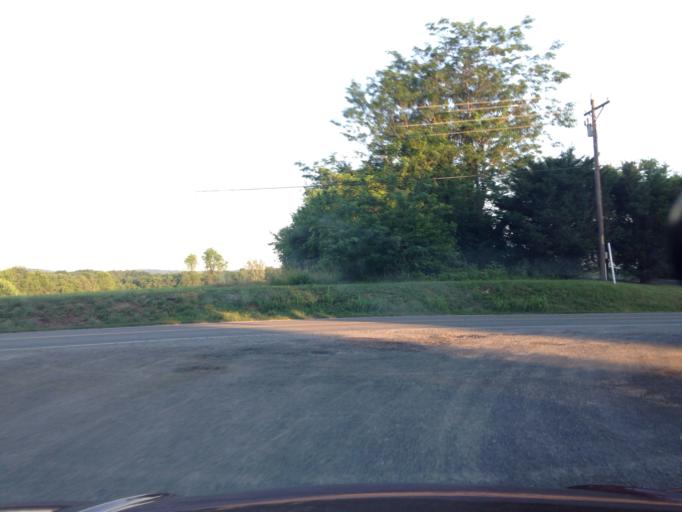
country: US
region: Virginia
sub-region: Loudoun County
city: Lovettsville
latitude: 39.2677
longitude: -77.6230
